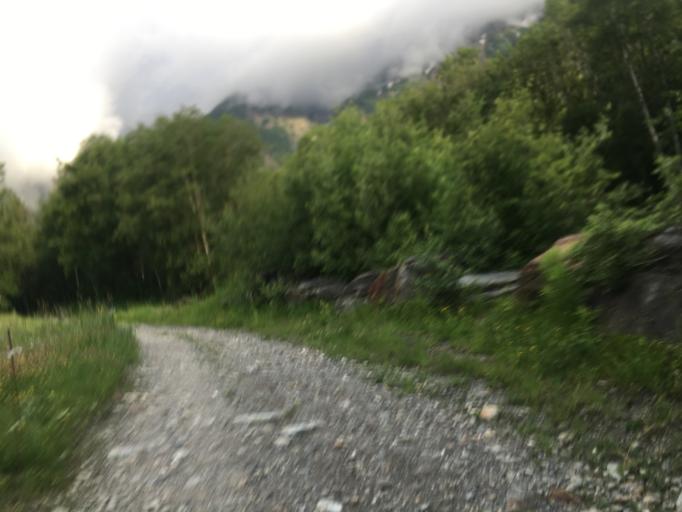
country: FR
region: Rhone-Alpes
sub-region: Departement de la Haute-Savoie
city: Les Houches
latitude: 45.8898
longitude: 6.8032
